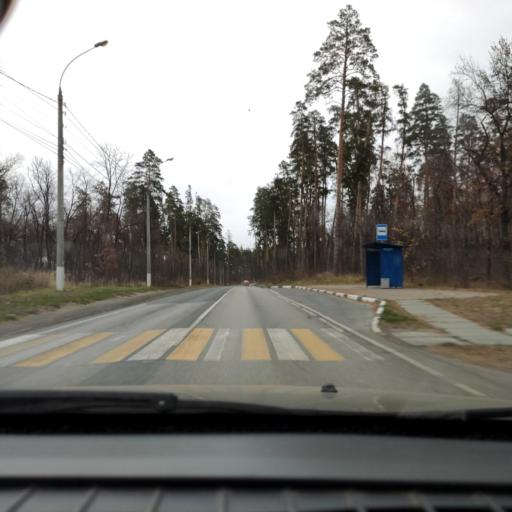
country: RU
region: Samara
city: Tol'yatti
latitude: 53.4924
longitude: 49.3008
